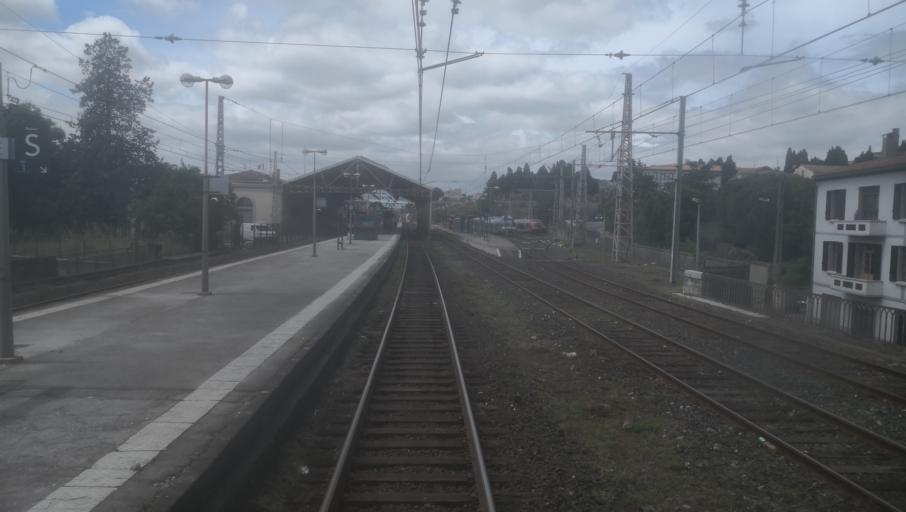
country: FR
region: Languedoc-Roussillon
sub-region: Departement de l'Aude
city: Carcassonne
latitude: 43.2183
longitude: 2.3520
